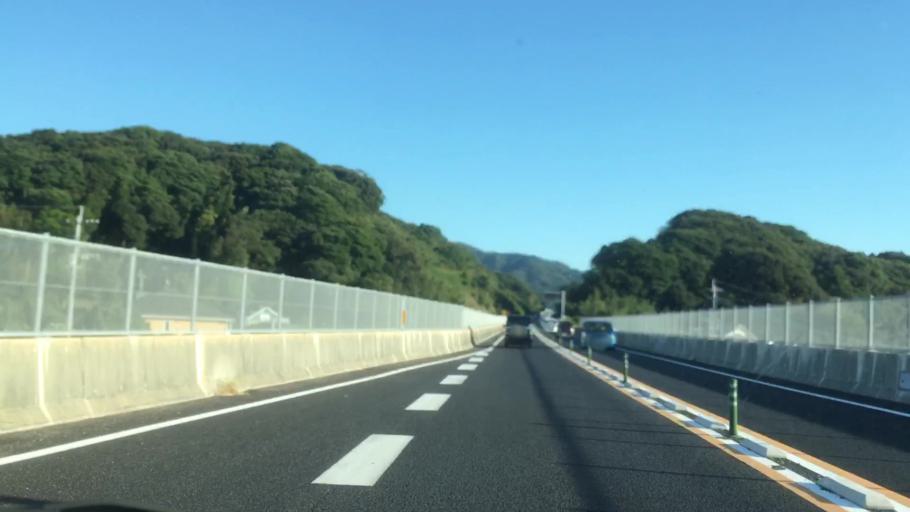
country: JP
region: Nagasaki
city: Sasebo
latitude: 33.2001
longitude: 129.6748
